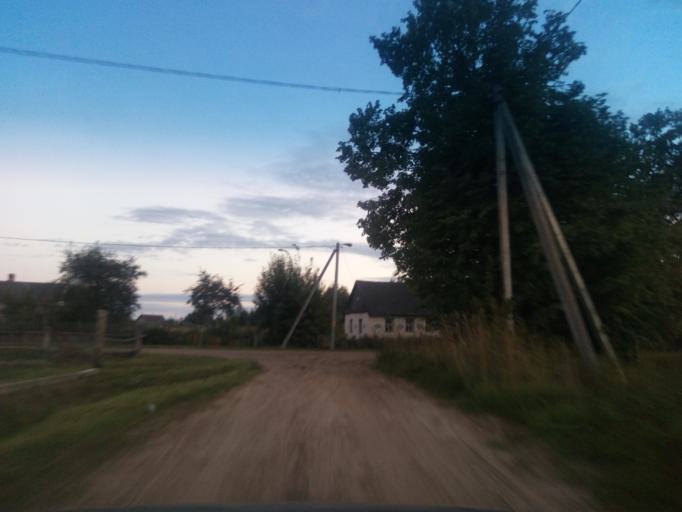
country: BY
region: Vitebsk
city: Dzisna
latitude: 55.6713
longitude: 28.3145
